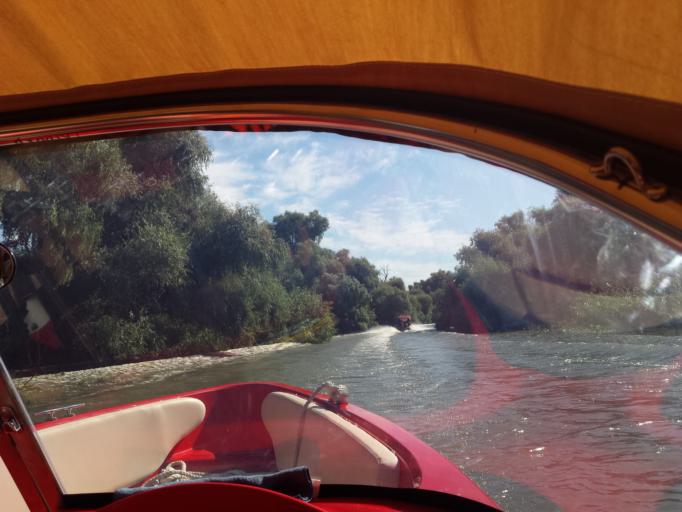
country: RO
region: Tulcea
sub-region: Comuna Pardina
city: Pardina
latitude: 45.2502
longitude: 29.0446
